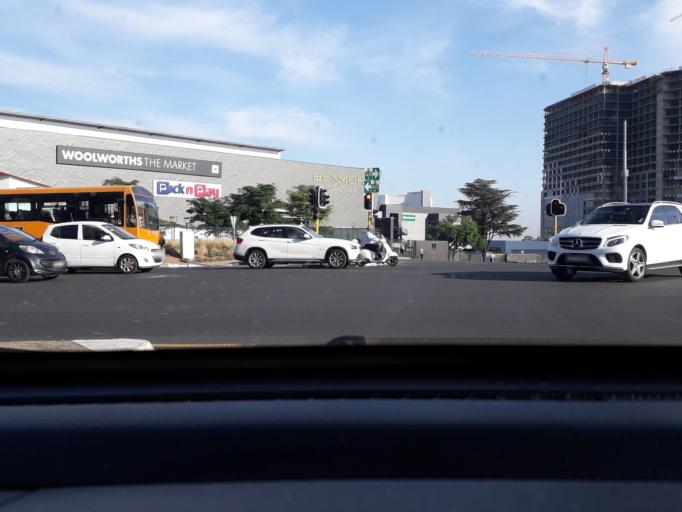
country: ZA
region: Gauteng
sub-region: City of Johannesburg Metropolitan Municipality
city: Johannesburg
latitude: -26.1010
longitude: 28.0505
